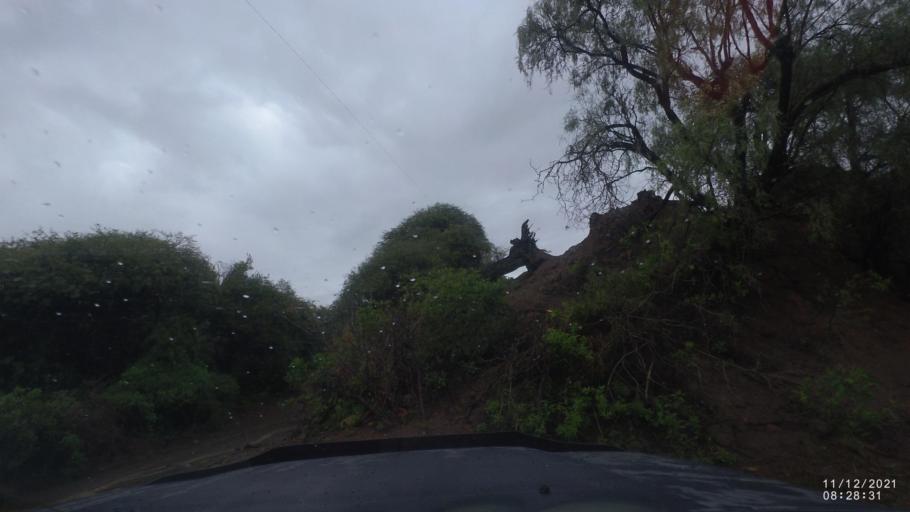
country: BO
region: Cochabamba
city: Tarata
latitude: -17.9393
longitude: -65.9310
